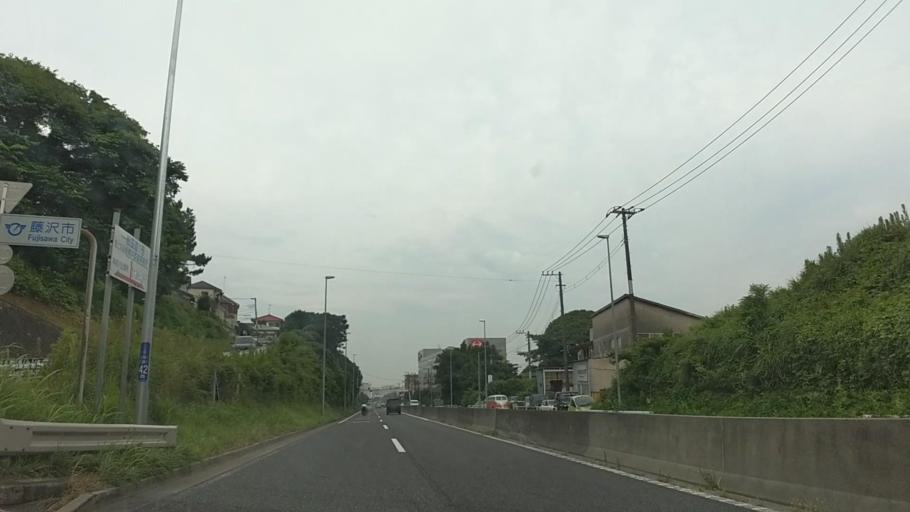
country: JP
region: Kanagawa
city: Fujisawa
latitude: 35.3591
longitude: 139.4927
